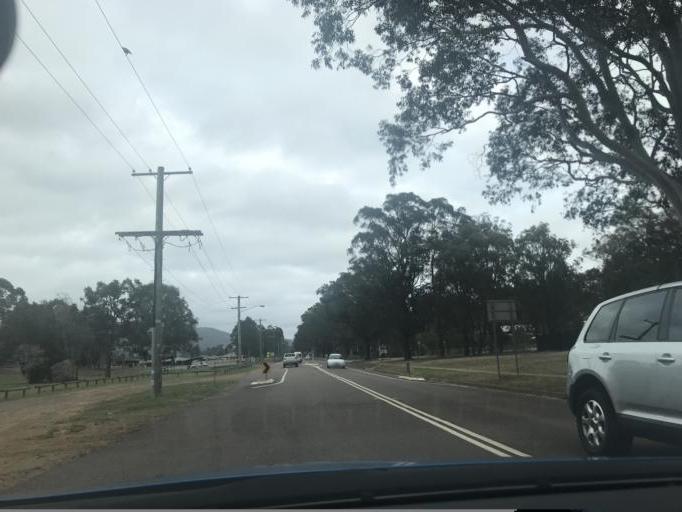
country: AU
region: New South Wales
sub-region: Cessnock
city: Cessnock
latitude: -32.8299
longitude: 151.3348
